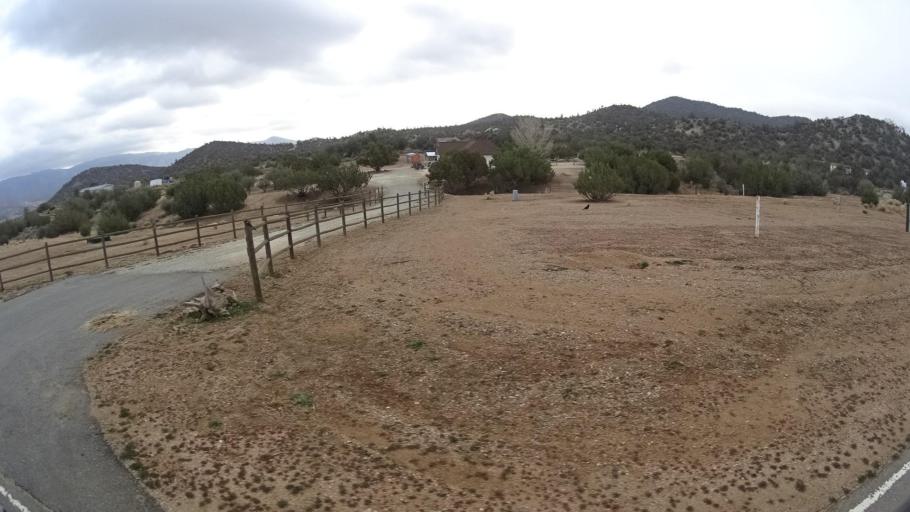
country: US
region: California
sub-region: Kern County
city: Tehachapi
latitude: 35.1748
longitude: -118.3577
